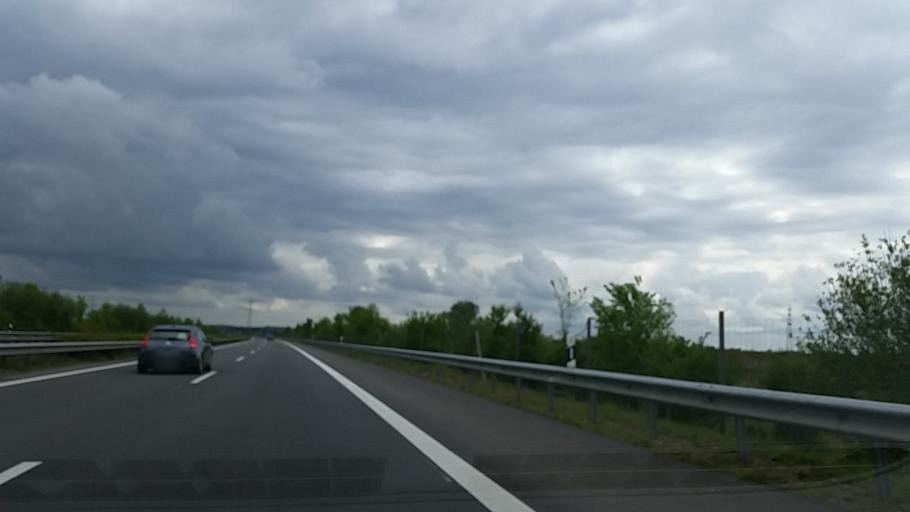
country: DE
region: Lower Saxony
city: Horneburg
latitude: 53.5272
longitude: 9.5804
